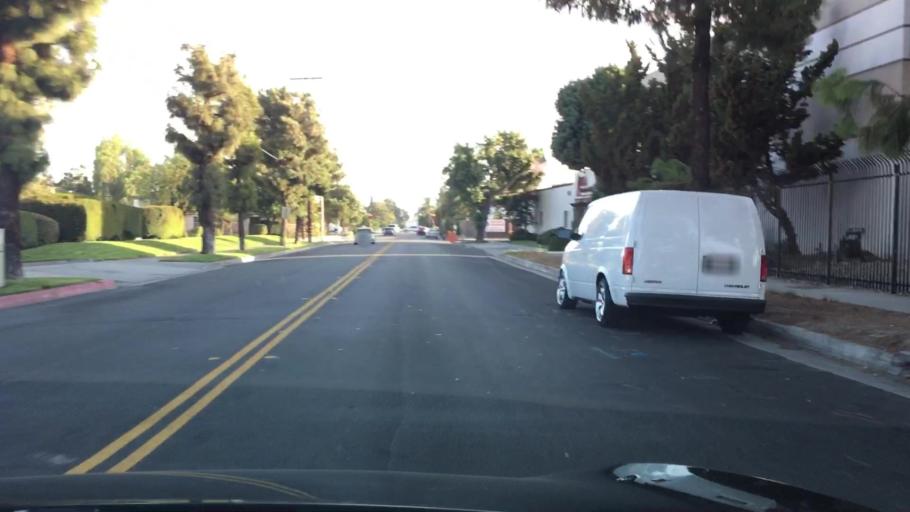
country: US
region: California
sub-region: San Bernardino County
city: Ontario
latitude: 34.0567
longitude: -117.6367
